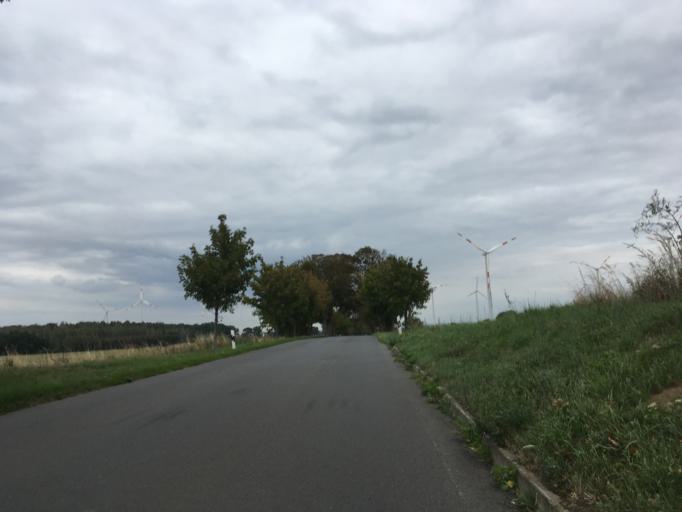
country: DE
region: Brandenburg
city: Passow
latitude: 53.0901
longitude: 14.1612
